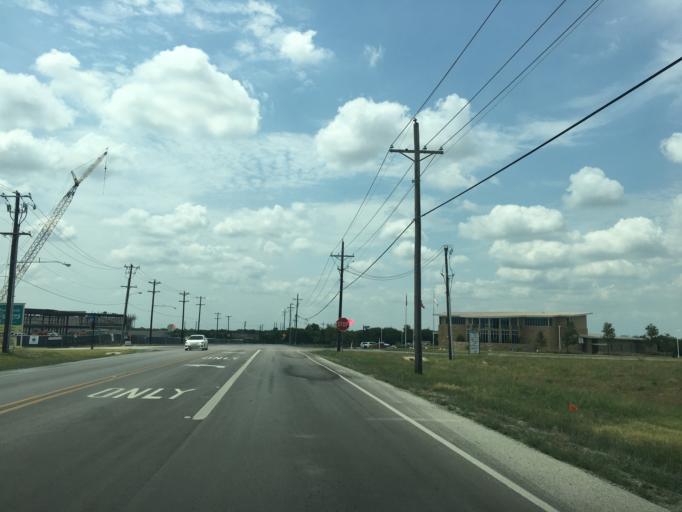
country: US
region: Texas
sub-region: Rockwall County
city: Fate
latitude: 32.9561
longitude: -96.3787
